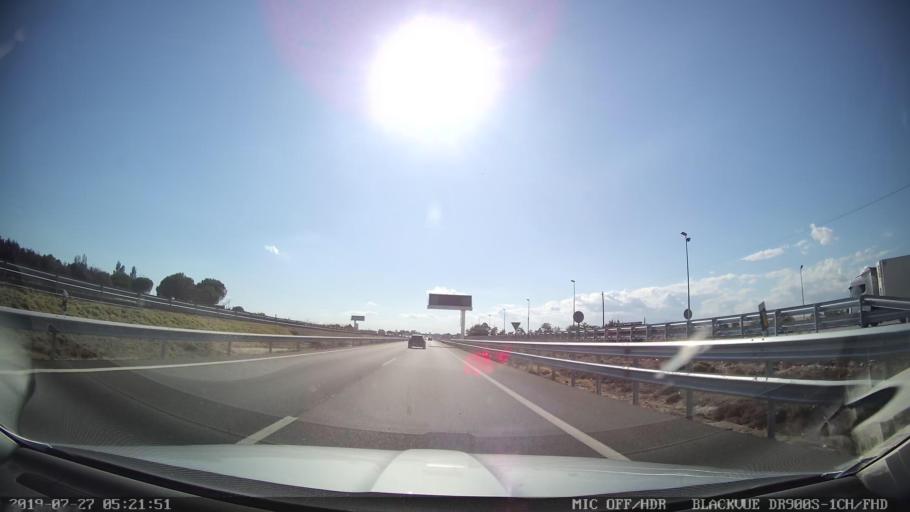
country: ES
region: Castille-La Mancha
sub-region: Province of Toledo
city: Otero
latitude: 40.0224
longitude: -4.4877
